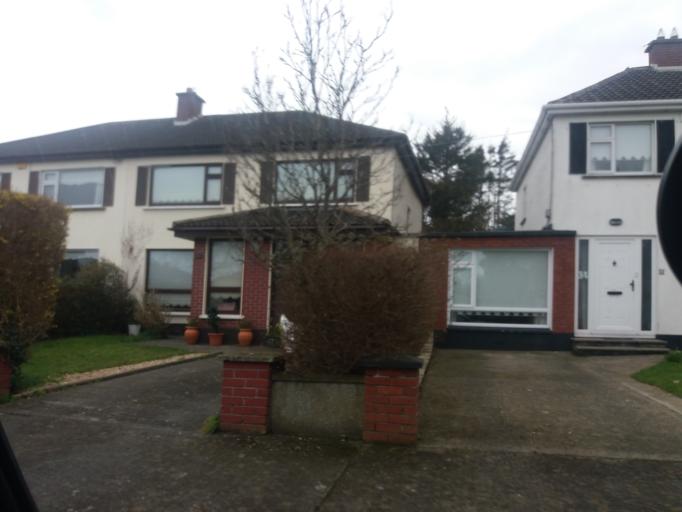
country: IE
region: Leinster
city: Portmarnock
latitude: 53.4322
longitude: -6.1322
